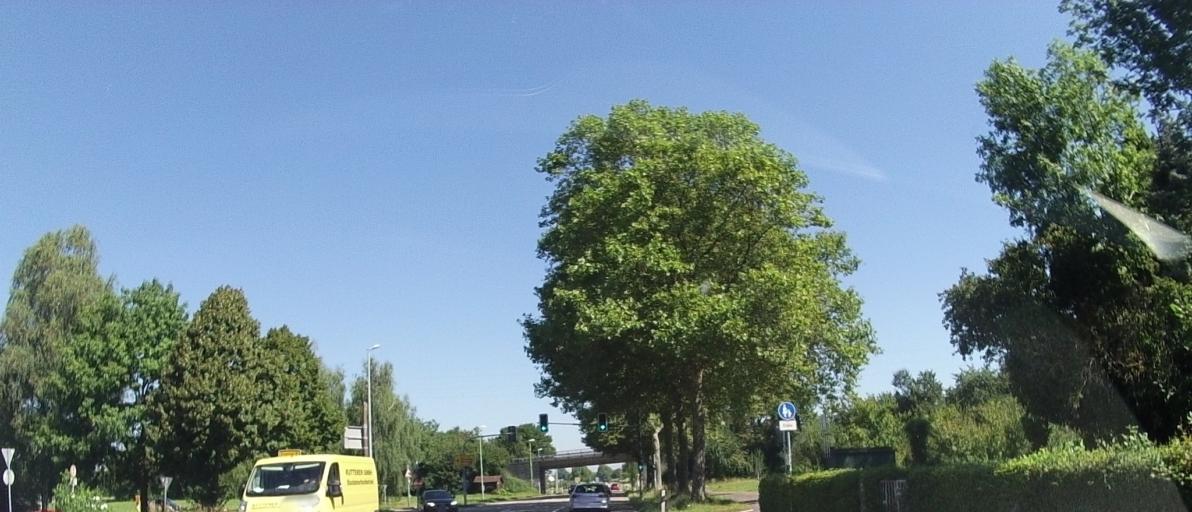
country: DE
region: Baden-Wuerttemberg
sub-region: Karlsruhe Region
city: Buhl
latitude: 48.7029
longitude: 8.1404
